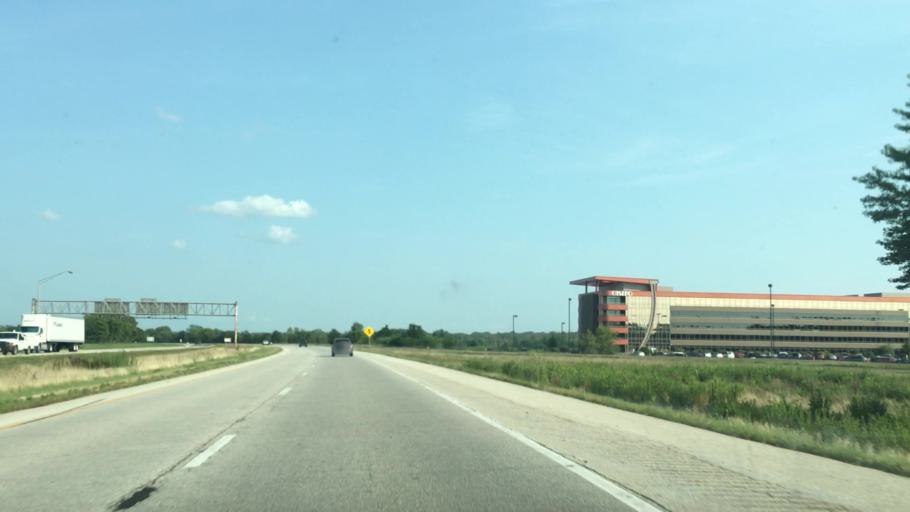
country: US
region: Illinois
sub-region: Rock Island County
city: Milan
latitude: 41.4621
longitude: -90.6131
